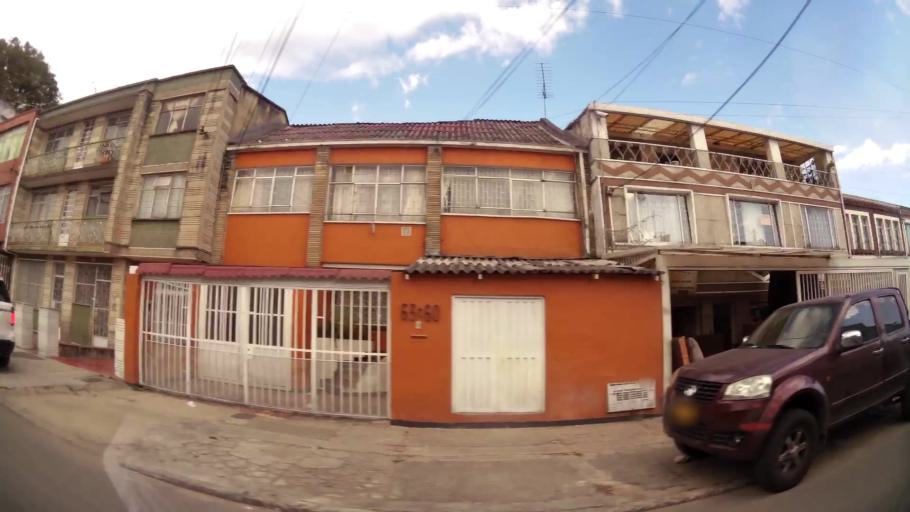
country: CO
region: Bogota D.C.
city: Bogota
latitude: 4.6538
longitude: -74.0695
